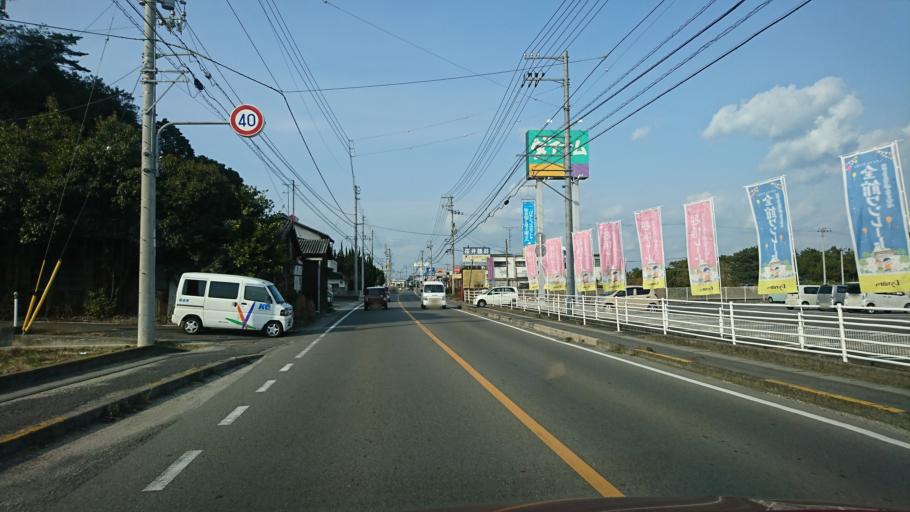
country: JP
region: Ehime
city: Saijo
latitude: 34.0299
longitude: 133.0366
